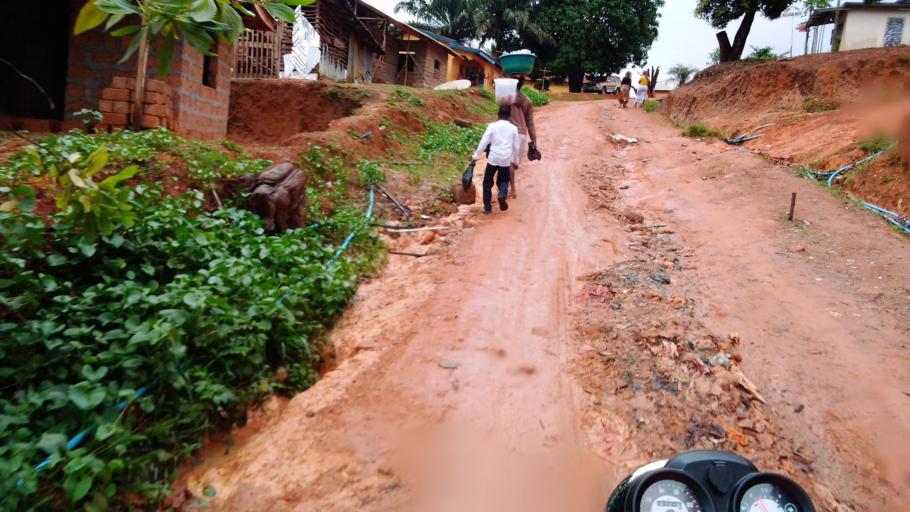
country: SL
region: Eastern Province
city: Kenema
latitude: 7.8966
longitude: -11.1860
